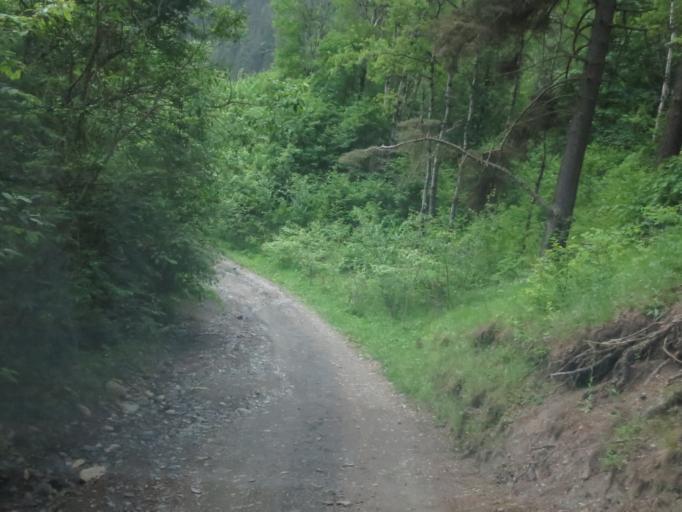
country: RU
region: Chechnya
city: Itum-Kali
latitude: 42.3620
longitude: 45.6507
